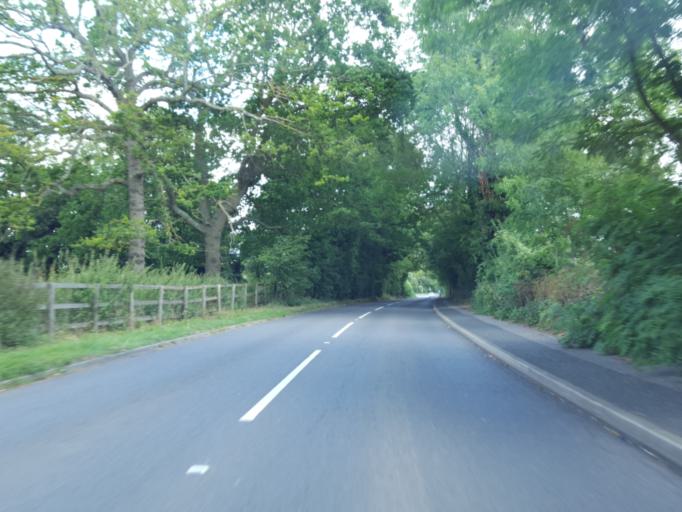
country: GB
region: England
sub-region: Kent
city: Kings Hill
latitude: 51.2825
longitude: 0.3966
